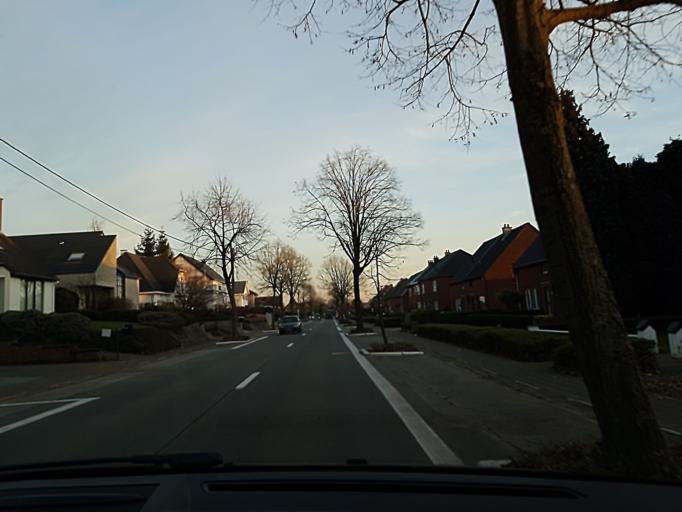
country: BE
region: Flanders
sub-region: Provincie Antwerpen
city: Bornem
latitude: 51.0932
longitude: 4.2473
